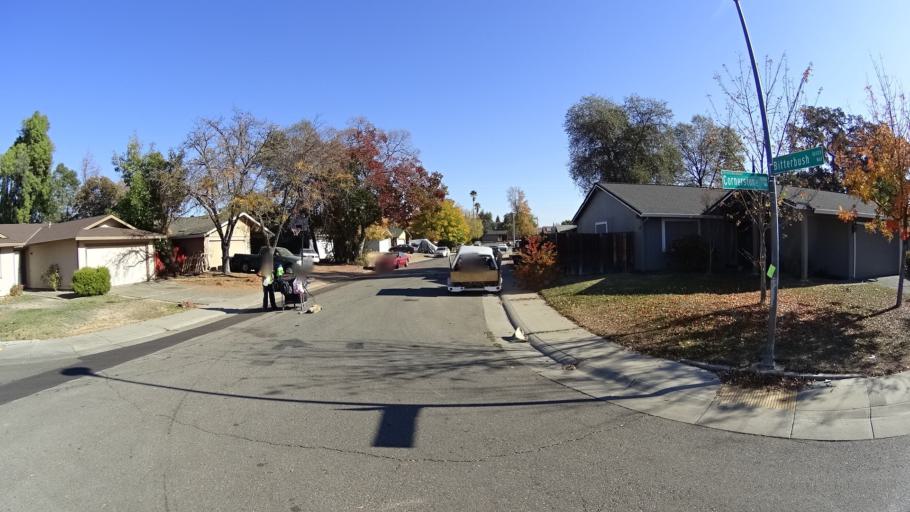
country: US
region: California
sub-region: Sacramento County
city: Antelope
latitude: 38.7133
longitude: -121.3127
